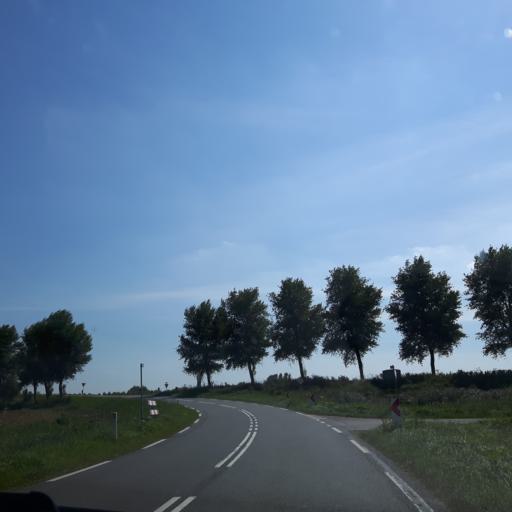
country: NL
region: North Brabant
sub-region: Gemeente Steenbergen
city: Nieuw-Vossemeer
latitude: 51.5706
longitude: 4.1826
